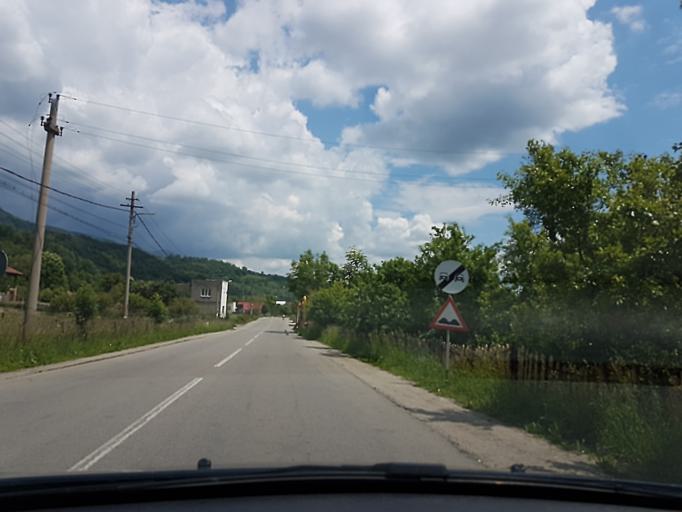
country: RO
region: Hunedoara
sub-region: Comuna Uricani
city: Uricani
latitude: 45.3347
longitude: 23.1312
